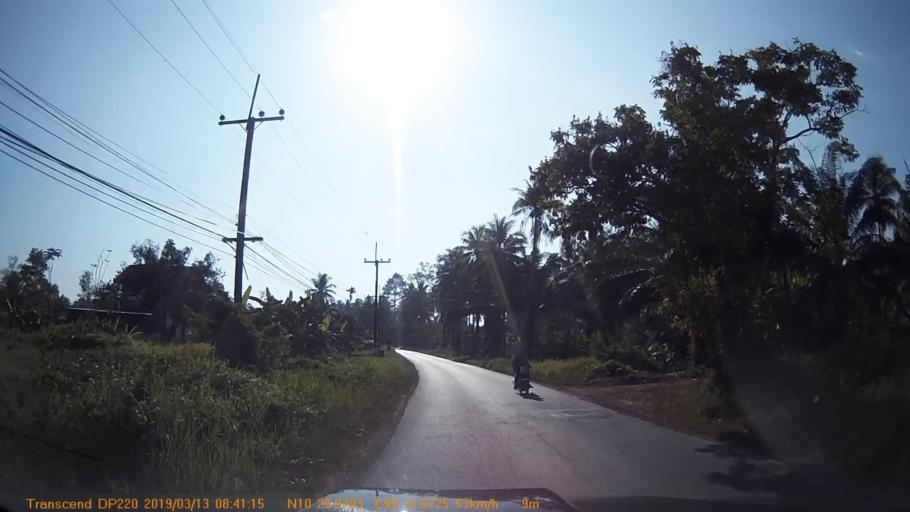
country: TH
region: Chumphon
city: Chumphon
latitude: 10.4994
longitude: 99.2114
